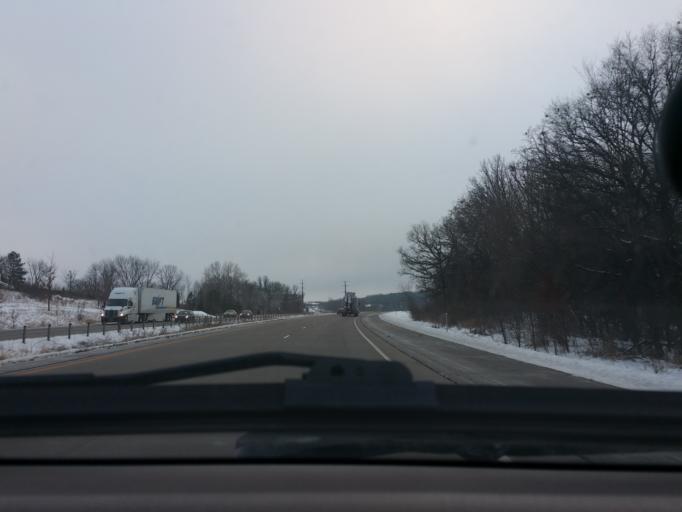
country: US
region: Minnesota
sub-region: Scott County
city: Elko New Market
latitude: 44.6065
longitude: -93.2968
